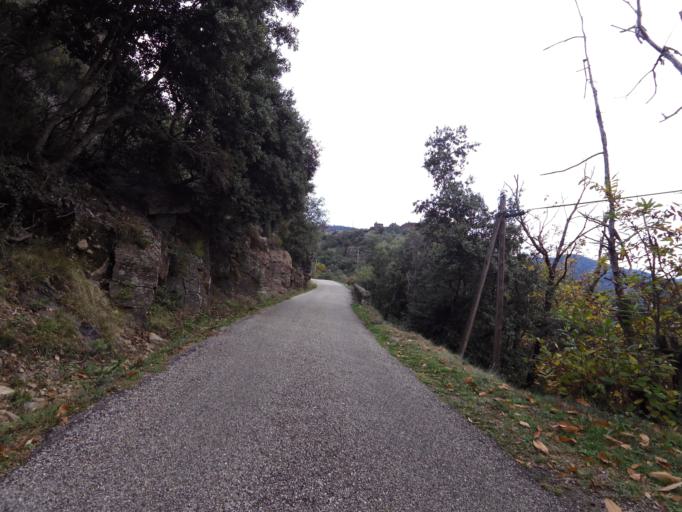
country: FR
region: Rhone-Alpes
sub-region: Departement de l'Ardeche
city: Les Vans
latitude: 44.4943
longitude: 4.0479
